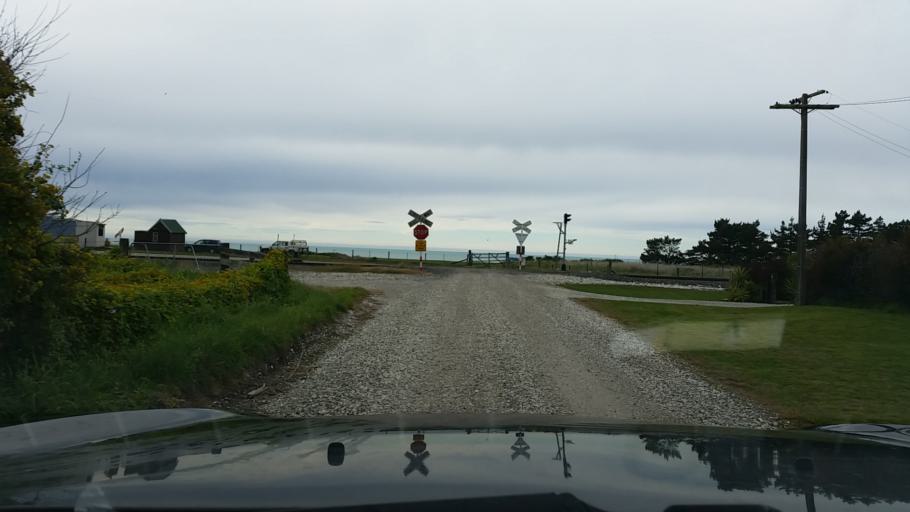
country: NZ
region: Marlborough
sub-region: Marlborough District
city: Blenheim
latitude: -41.9241
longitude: 174.0931
